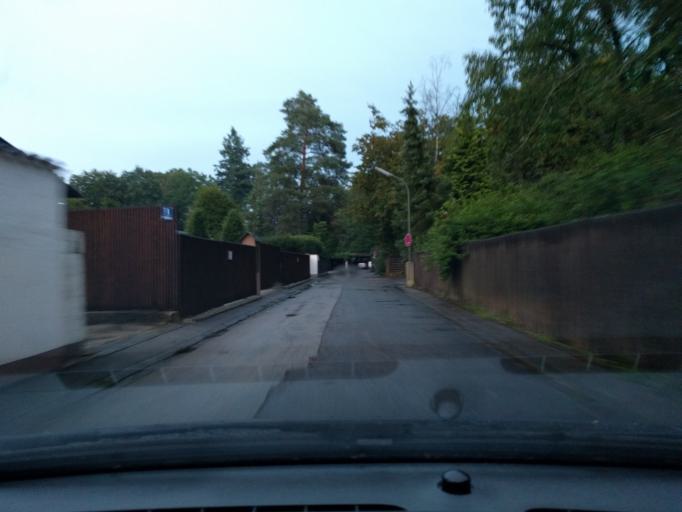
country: DE
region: Bavaria
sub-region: Upper Bavaria
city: Pullach im Isartal
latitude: 48.0531
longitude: 11.5371
